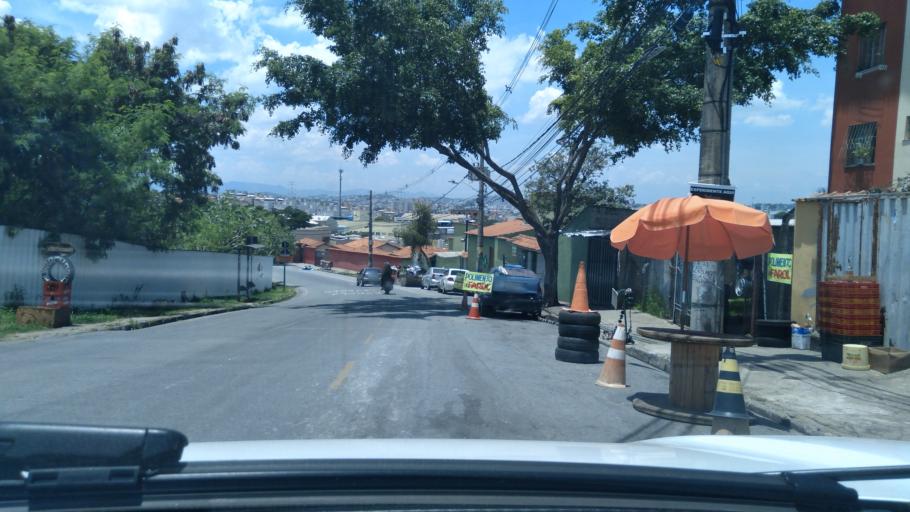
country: BR
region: Minas Gerais
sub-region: Contagem
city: Contagem
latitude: -19.9279
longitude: -44.0160
